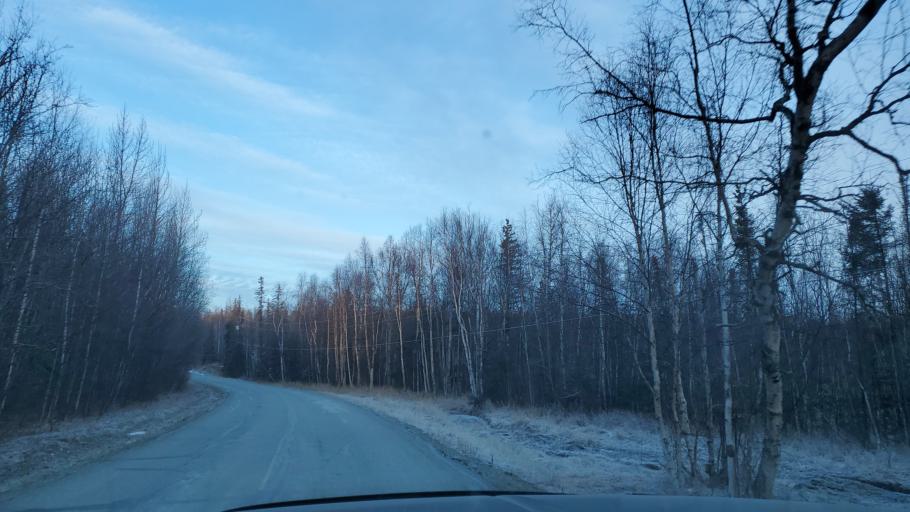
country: US
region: Alaska
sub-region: Matanuska-Susitna Borough
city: Lakes
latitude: 61.6023
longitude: -149.3166
